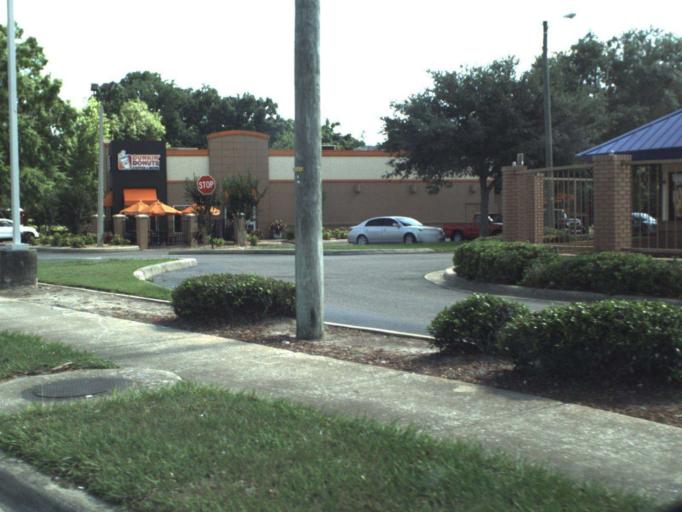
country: US
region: Florida
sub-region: Marion County
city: Ocala
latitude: 29.1708
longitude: -82.1400
